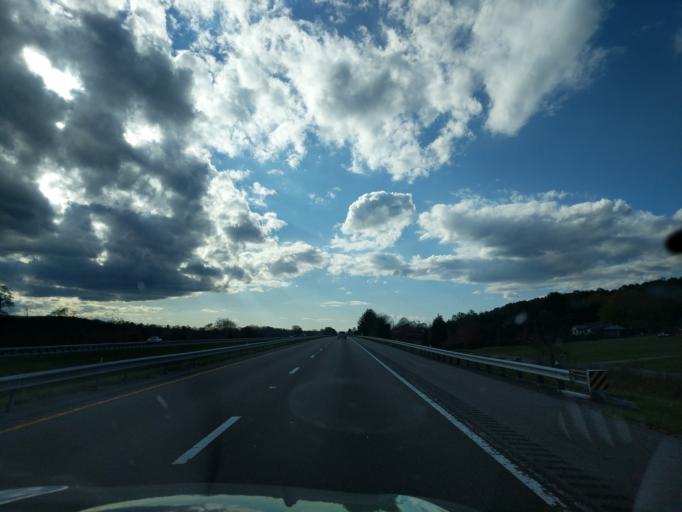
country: US
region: Virginia
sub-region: Wythe County
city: Rural Retreat
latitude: 36.9200
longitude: -81.2411
